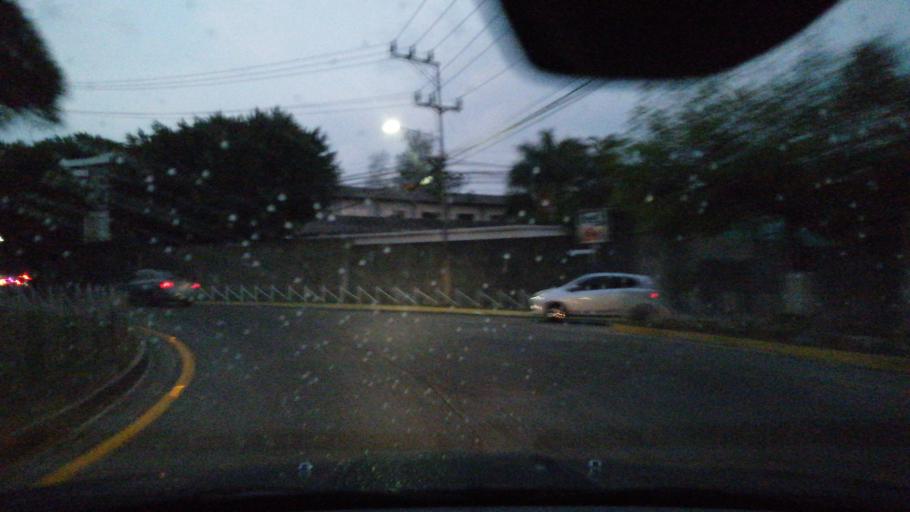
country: SV
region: San Salvador
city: San Salvador
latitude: 13.7105
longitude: -89.2037
